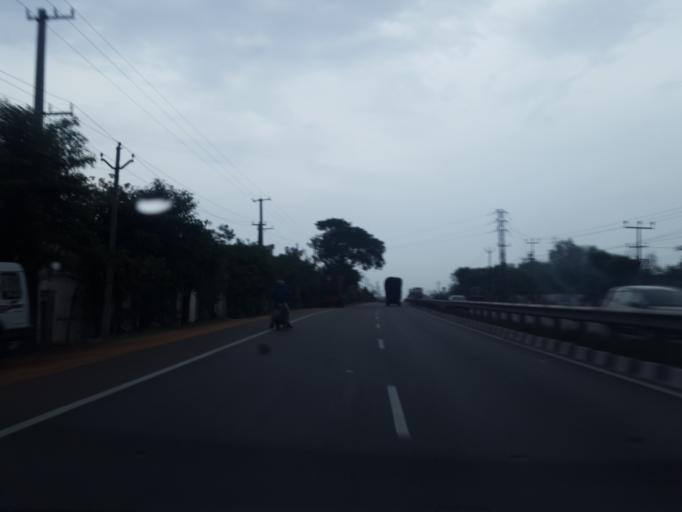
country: IN
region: Telangana
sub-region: Rangareddi
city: Sriramnagar
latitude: 17.1595
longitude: 78.2950
